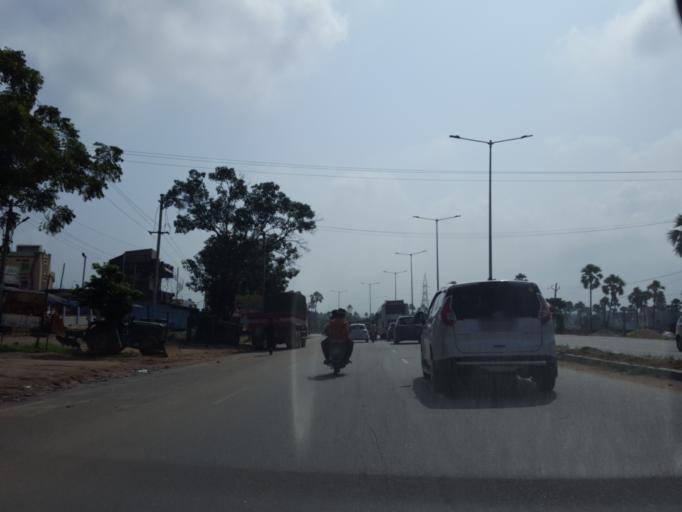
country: IN
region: Telangana
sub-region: Rangareddi
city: Lal Bahadur Nagar
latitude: 17.3097
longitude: 78.6876
